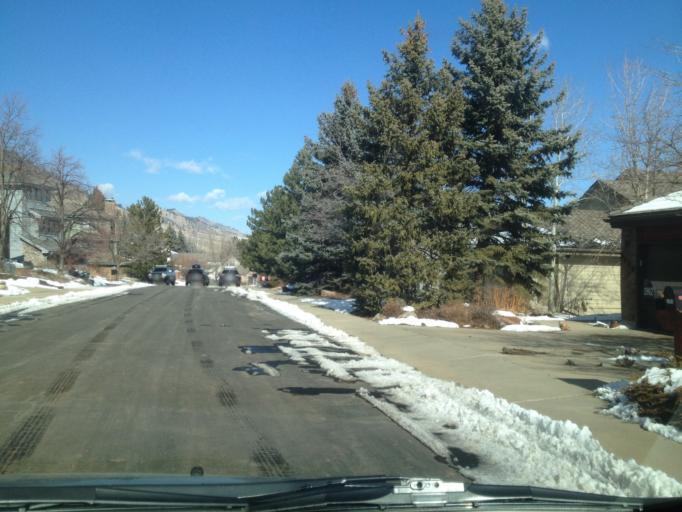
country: US
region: Colorado
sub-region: Boulder County
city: Boulder
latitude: 40.0455
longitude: -105.2937
